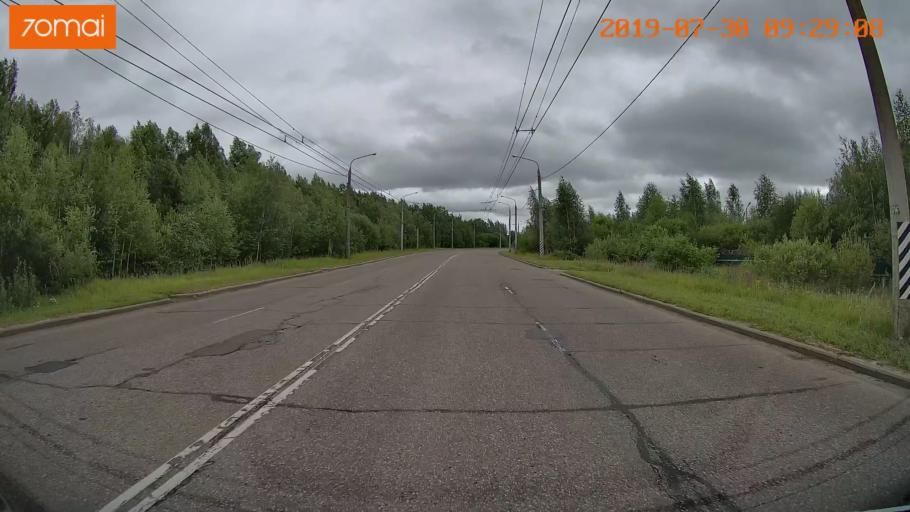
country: RU
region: Ivanovo
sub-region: Gorod Ivanovo
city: Ivanovo
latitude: 56.9467
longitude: 40.9469
